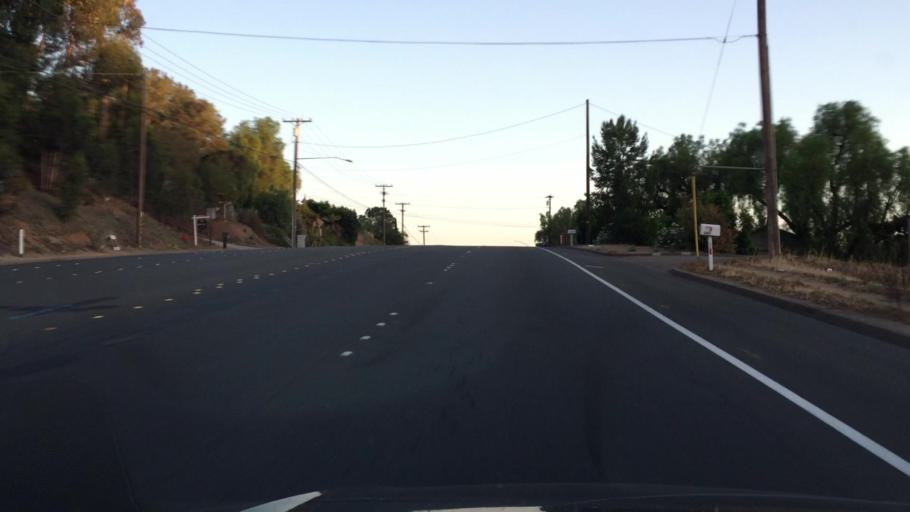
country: US
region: California
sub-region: San Diego County
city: Bostonia
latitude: 32.7777
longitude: -116.9280
